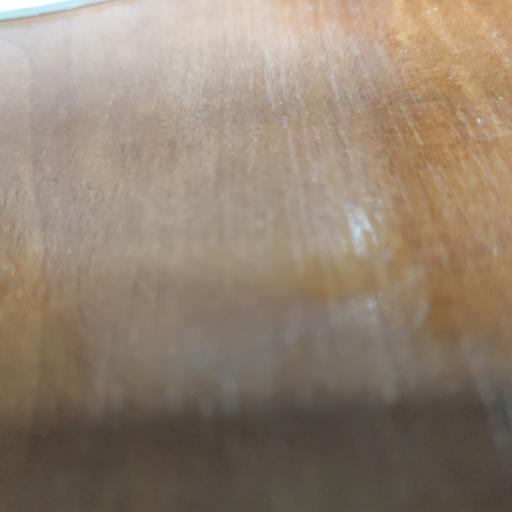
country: LV
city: Tervete
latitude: 56.4783
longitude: 23.4220
